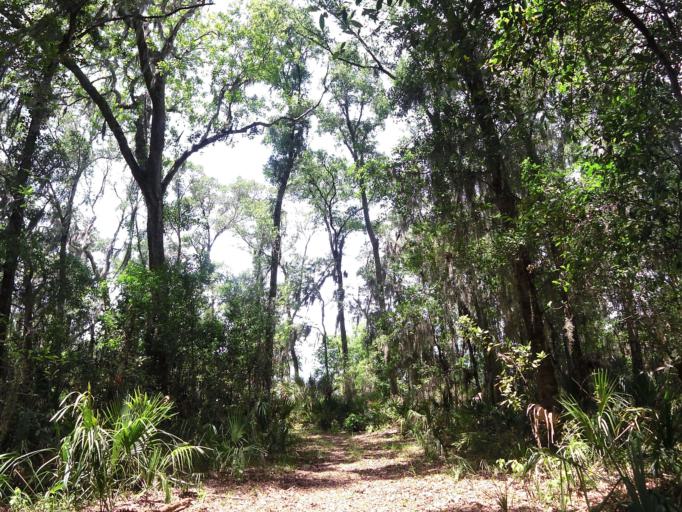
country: US
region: Florida
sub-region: Nassau County
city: Fernandina Beach
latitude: 30.4945
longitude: -81.4886
